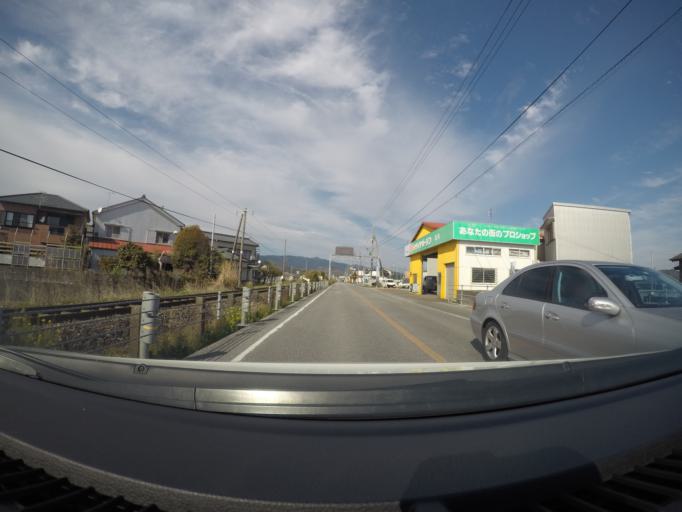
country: JP
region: Kochi
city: Kochi-shi
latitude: 33.5983
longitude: 133.6704
